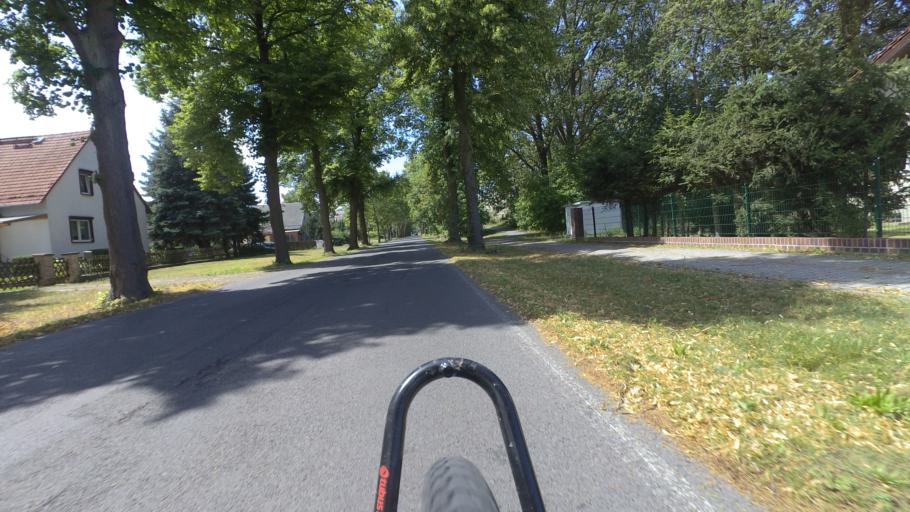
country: DE
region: Brandenburg
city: Ludwigsfelde
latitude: 52.3135
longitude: 13.2981
